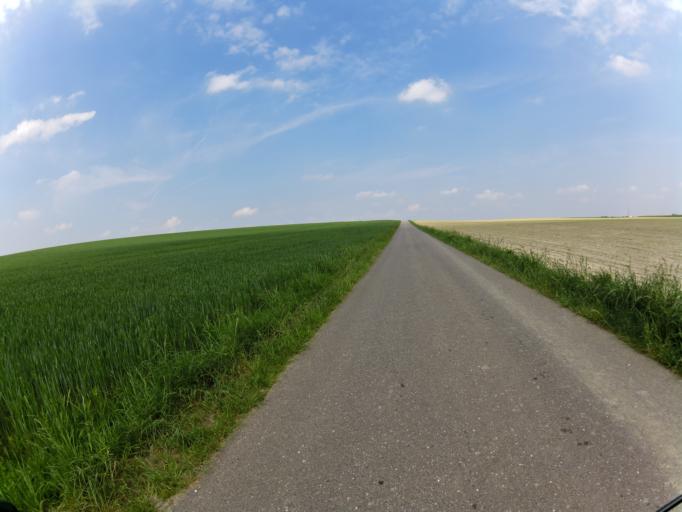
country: DE
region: North Rhine-Westphalia
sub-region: Regierungsbezirk Koln
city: Gangelt
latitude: 50.9926
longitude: 6.0229
